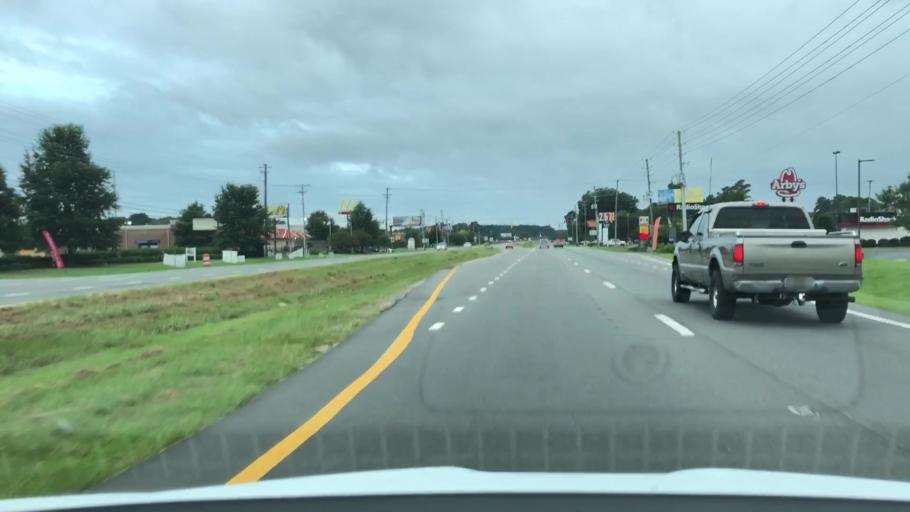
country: US
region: North Carolina
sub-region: Lenoir County
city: Kinston
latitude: 35.2621
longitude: -77.6460
